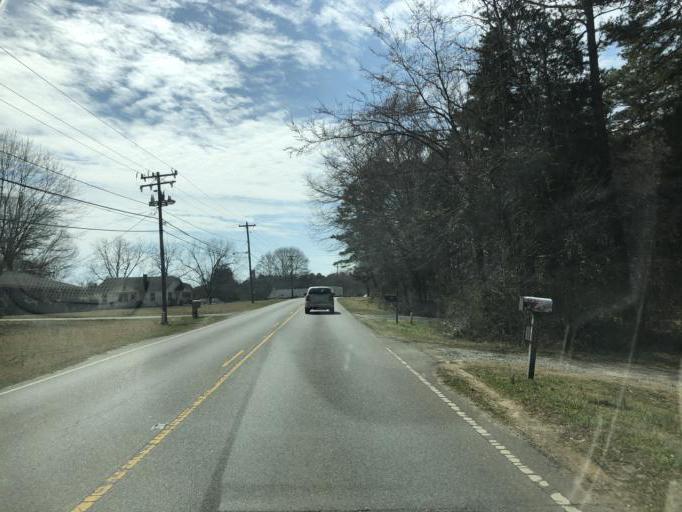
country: US
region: North Carolina
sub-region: Gaston County
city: Stanley
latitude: 35.3360
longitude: -81.1184
